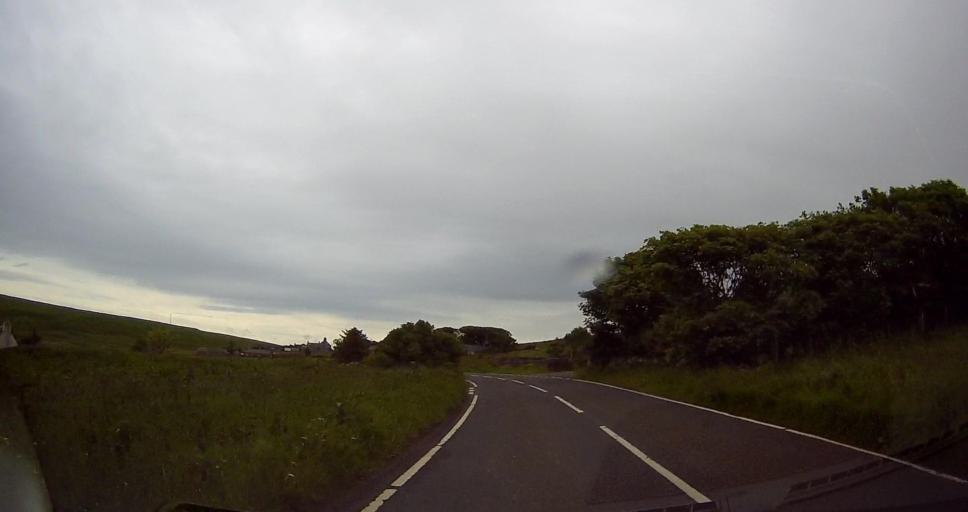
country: GB
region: Scotland
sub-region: Orkney Islands
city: Orkney
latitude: 59.1080
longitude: -3.0942
